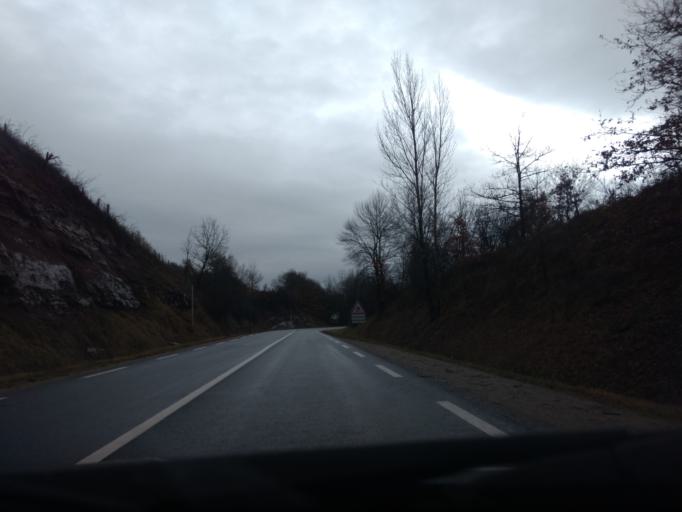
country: FR
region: Midi-Pyrenees
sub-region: Departement de l'Aveyron
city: Firmi
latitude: 44.5110
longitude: 2.3608
